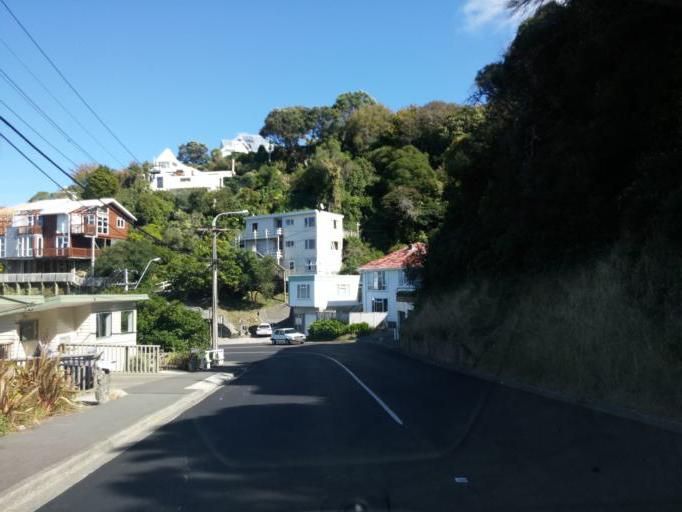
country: NZ
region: Wellington
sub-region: Wellington City
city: Kelburn
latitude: -41.2919
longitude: 174.7594
